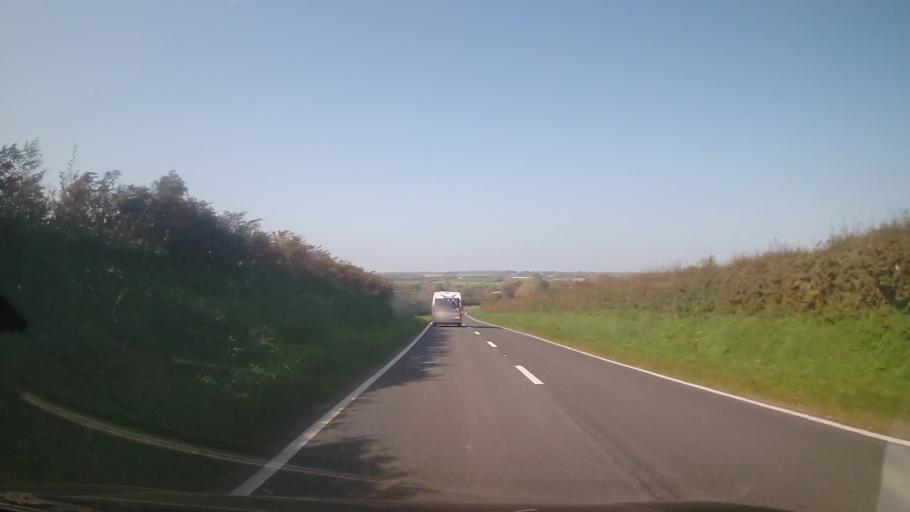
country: GB
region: Wales
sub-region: County of Ceredigion
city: Cardigan
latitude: 52.0306
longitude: -4.6936
